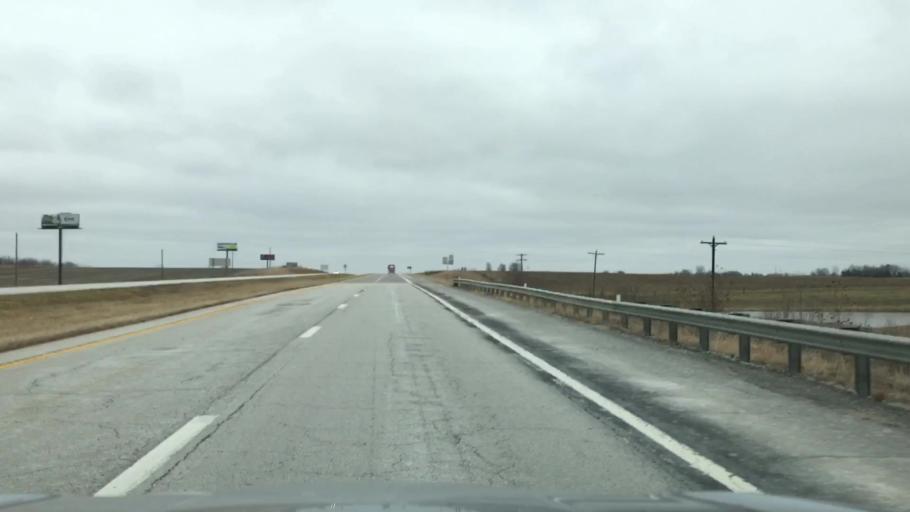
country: US
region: Missouri
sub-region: Caldwell County
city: Hamilton
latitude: 39.7334
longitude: -93.9957
